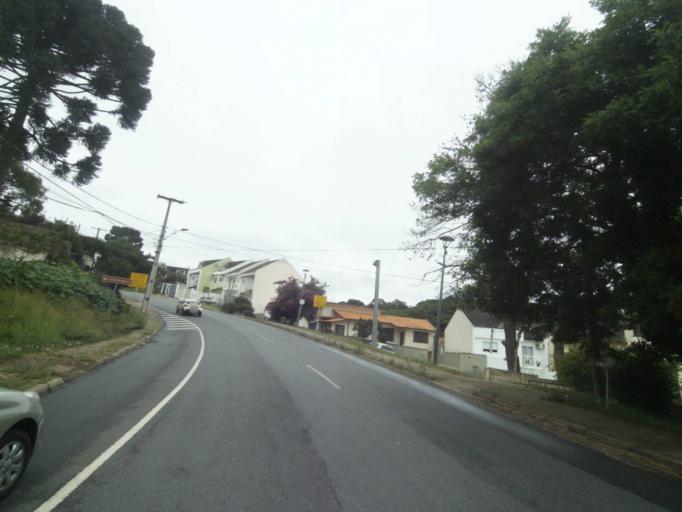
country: BR
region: Parana
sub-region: Curitiba
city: Curitiba
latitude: -25.4131
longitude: -49.2864
